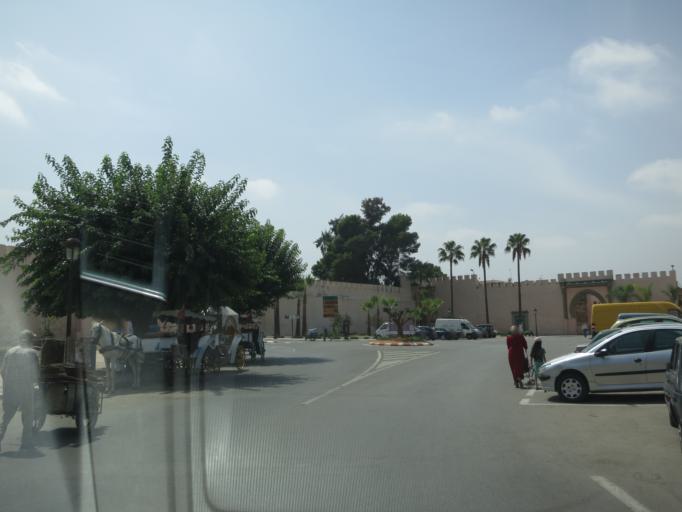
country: MA
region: Meknes-Tafilalet
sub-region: Meknes
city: Meknes
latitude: 33.8912
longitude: -5.5639
